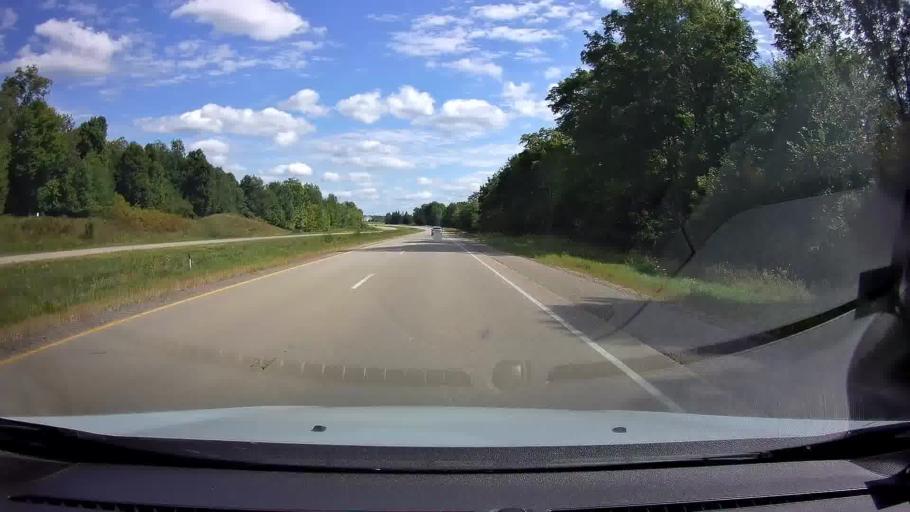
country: US
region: Wisconsin
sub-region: Shawano County
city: Wittenberg
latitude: 44.8075
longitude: -89.0367
